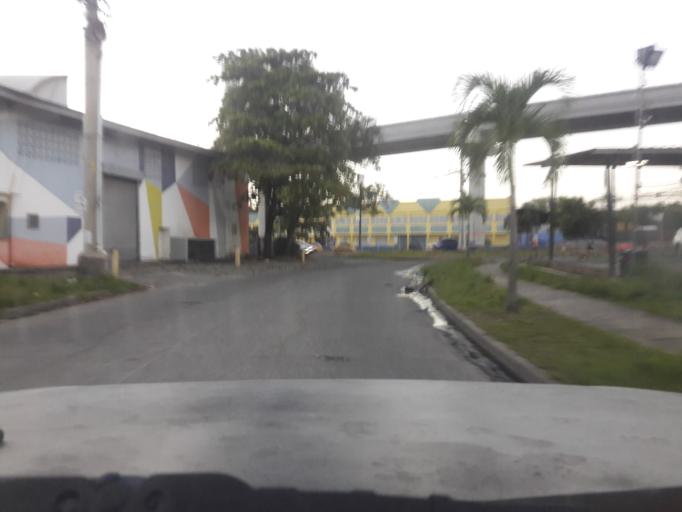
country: PA
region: Panama
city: San Miguelito
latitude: 9.0545
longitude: -79.4382
